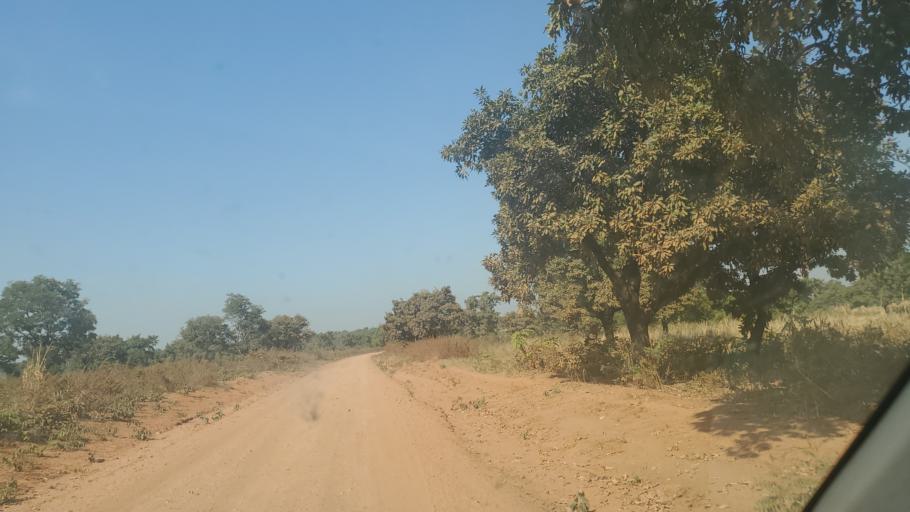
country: NG
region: Niger
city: Badeggi
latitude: 9.1227
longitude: 6.1930
